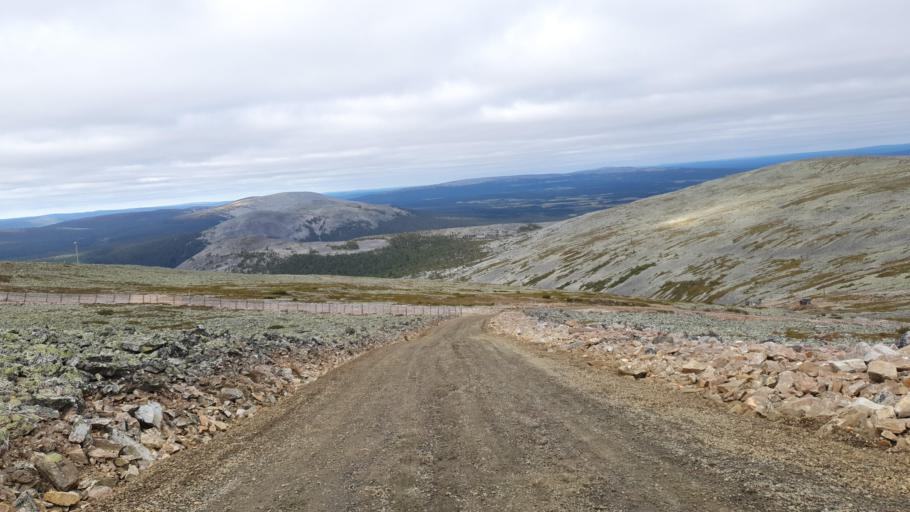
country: FI
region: Lapland
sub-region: Tunturi-Lappi
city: Kolari
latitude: 67.5700
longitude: 24.2149
